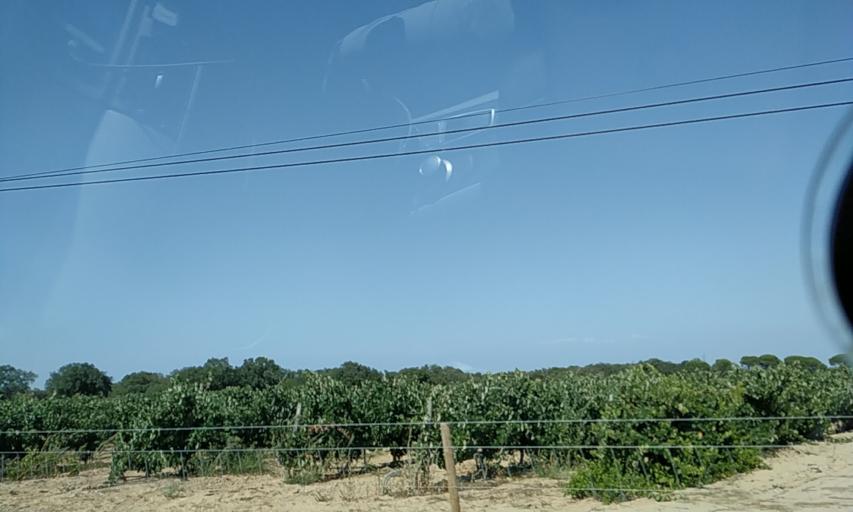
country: PT
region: Evora
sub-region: Vendas Novas
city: Vendas Novas
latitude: 38.7418
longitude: -8.6281
